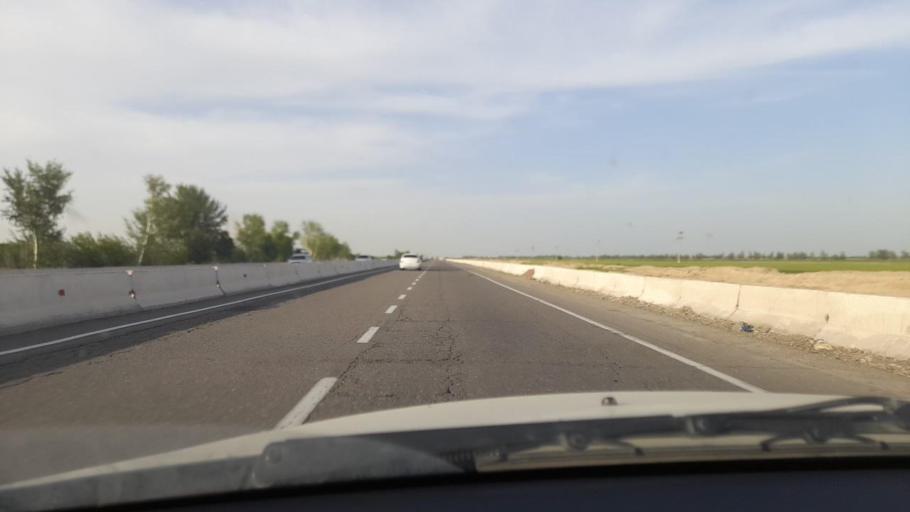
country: UZ
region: Jizzax
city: Paxtakor
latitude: 40.3391
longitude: 68.1174
